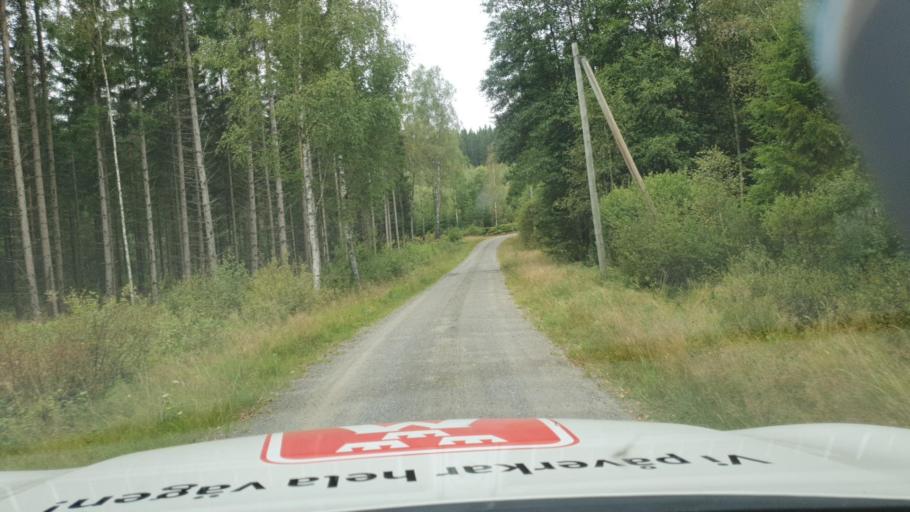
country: SE
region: Vaestra Goetaland
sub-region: Harryda Kommun
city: Hindas
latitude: 57.6900
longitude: 12.4691
